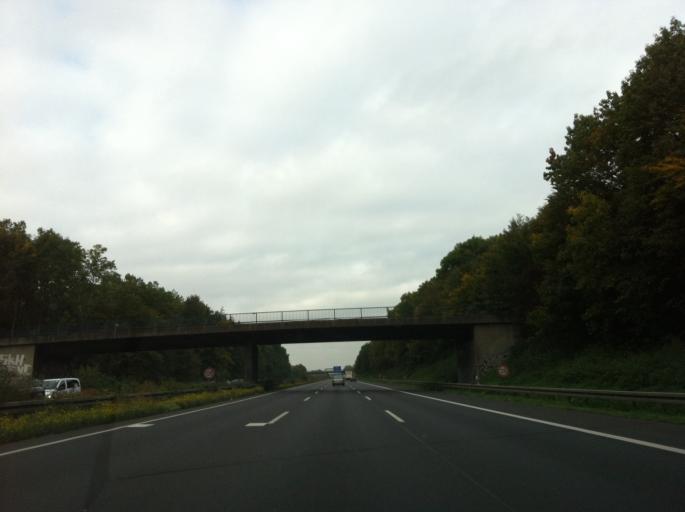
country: DE
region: North Rhine-Westphalia
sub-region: Regierungsbezirk Koln
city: Hurth
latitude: 50.9088
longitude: 6.8868
